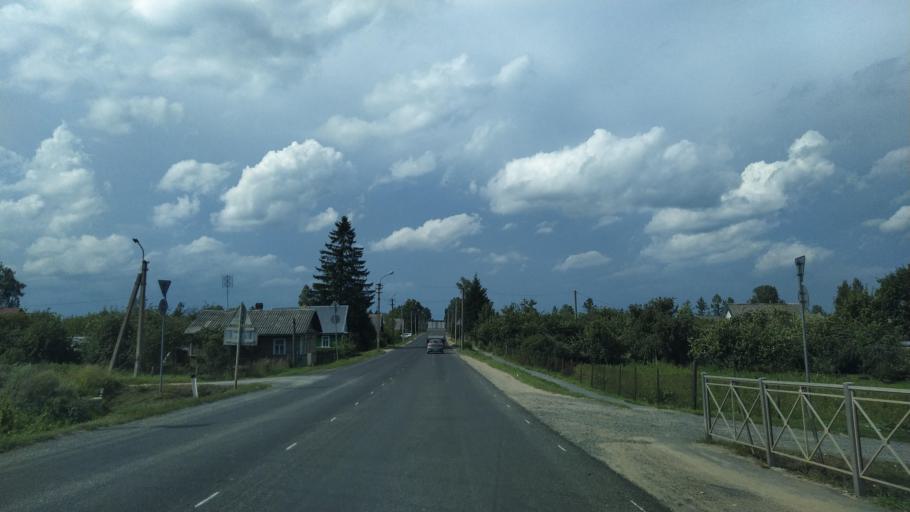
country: RU
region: Pskov
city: Porkhov
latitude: 57.7726
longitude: 29.5499
